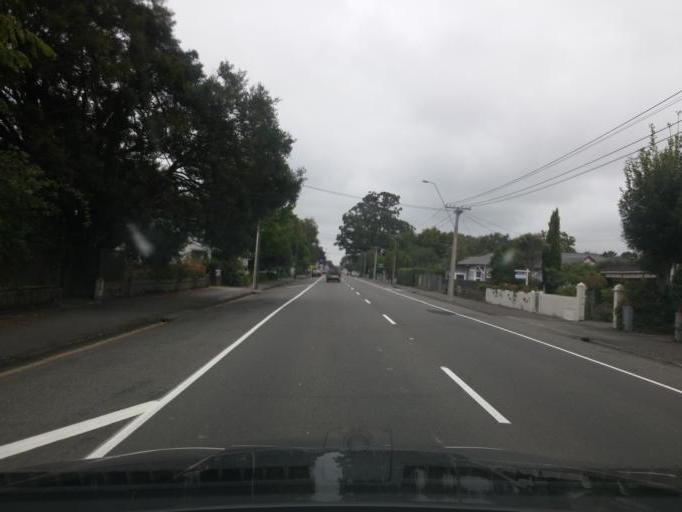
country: NZ
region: Wellington
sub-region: Masterton District
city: Masterton
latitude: -41.0842
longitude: 175.4561
